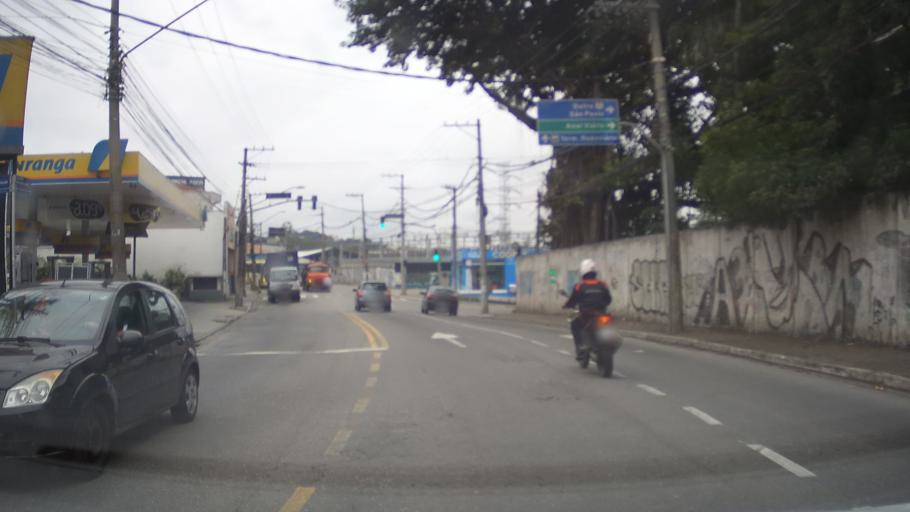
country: BR
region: Sao Paulo
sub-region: Guarulhos
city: Guarulhos
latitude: -23.4684
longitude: -46.5160
